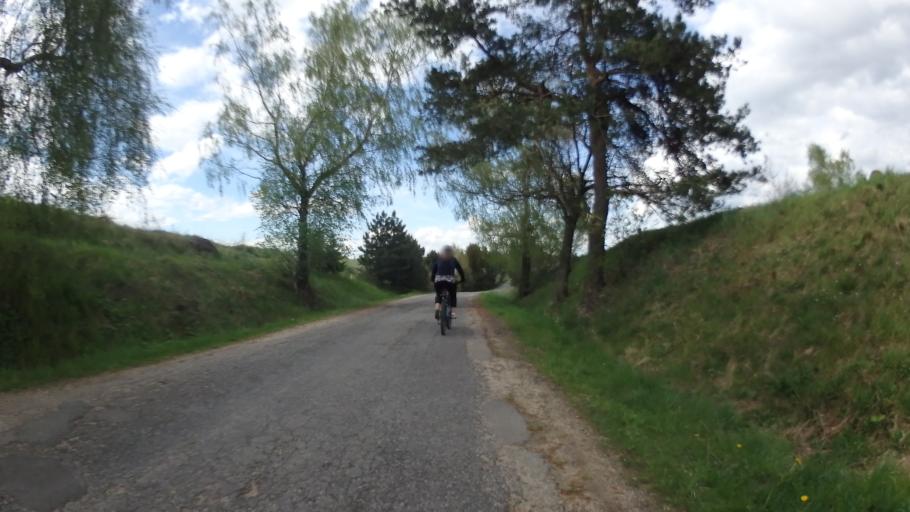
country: CZ
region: Vysocina
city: Merin
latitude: 49.3530
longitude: 15.9352
